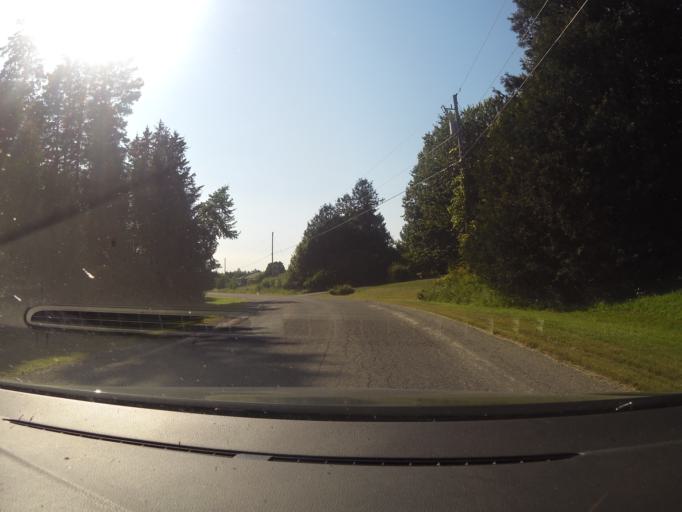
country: CA
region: Ontario
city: Carleton Place
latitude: 45.2978
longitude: -76.0752
